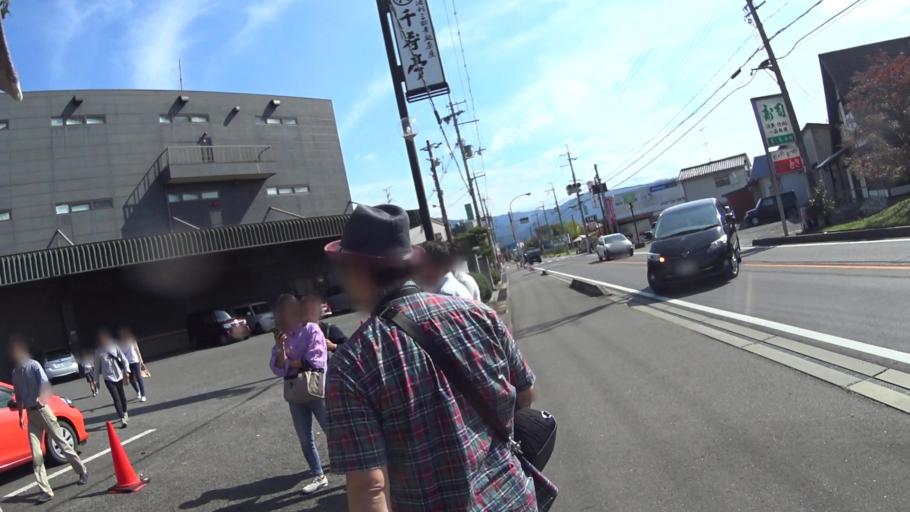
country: JP
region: Nara
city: Sakurai
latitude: 34.5327
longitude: 135.8407
